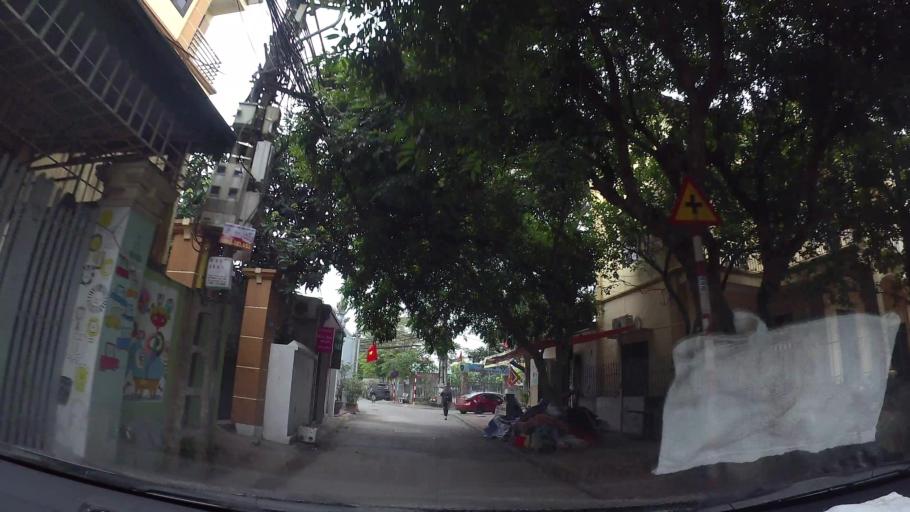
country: VN
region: Hung Yen
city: Van Giang
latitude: 20.9799
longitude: 105.8955
